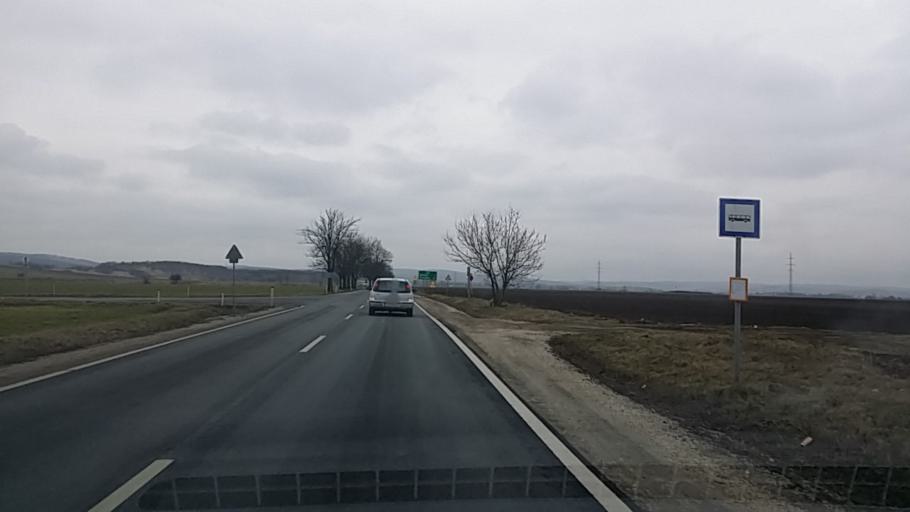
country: HU
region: Borsod-Abauj-Zemplen
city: Mucsony
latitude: 48.2600
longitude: 20.7223
